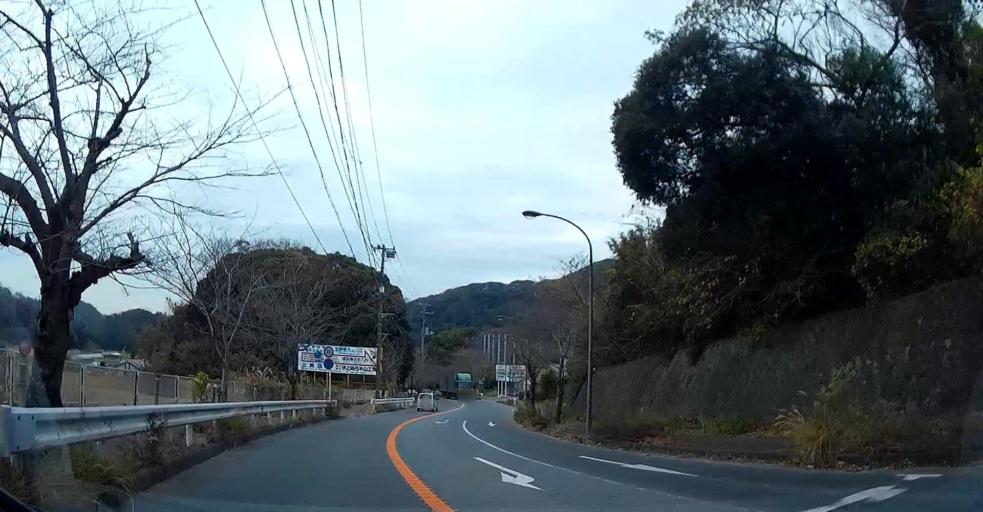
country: JP
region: Kanagawa
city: Yokosuka
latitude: 35.2236
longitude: 139.6636
